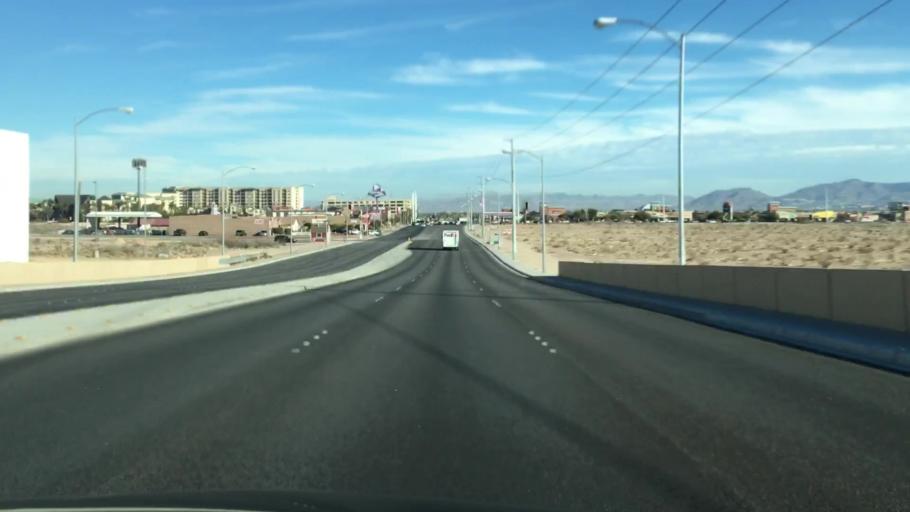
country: US
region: Nevada
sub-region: Clark County
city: Paradise
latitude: 36.0570
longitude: -115.1791
